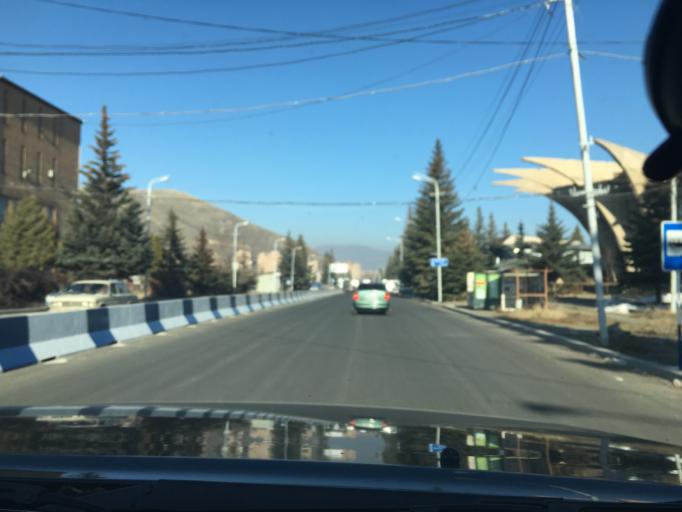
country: AM
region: Kotayk'i Marz
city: Hrazdan
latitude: 40.5151
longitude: 44.7545
